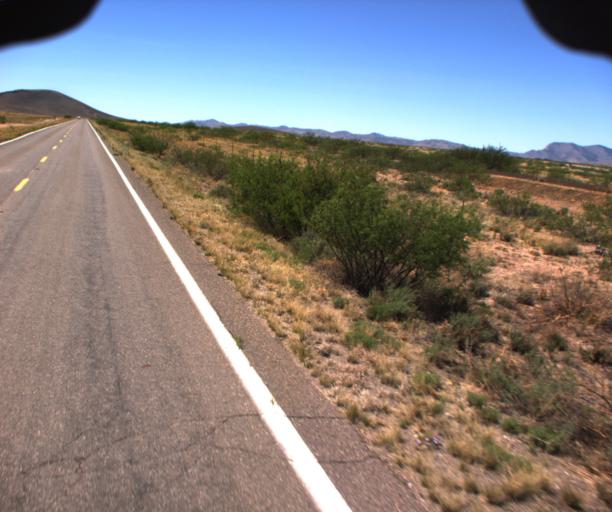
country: US
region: Arizona
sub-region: Cochise County
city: Douglas
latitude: 31.6474
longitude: -109.1666
